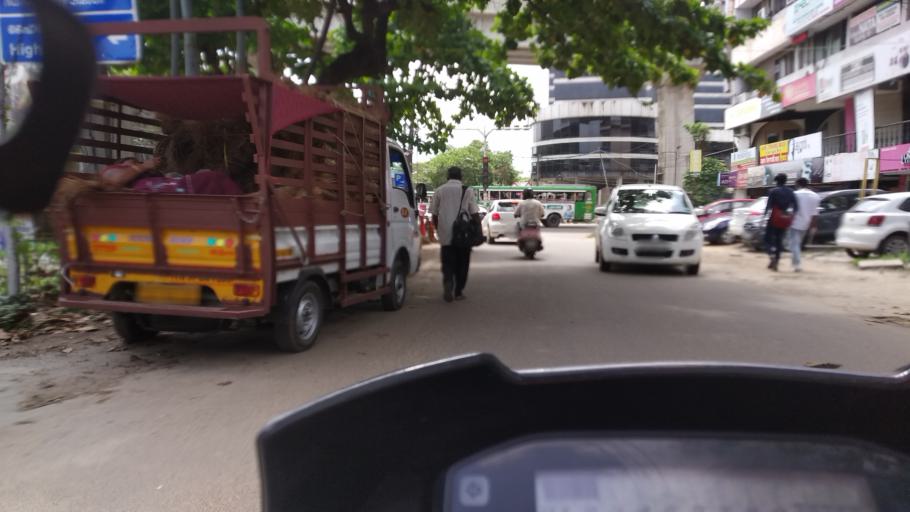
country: IN
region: Kerala
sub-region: Ernakulam
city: Cochin
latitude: 9.9919
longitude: 76.2899
